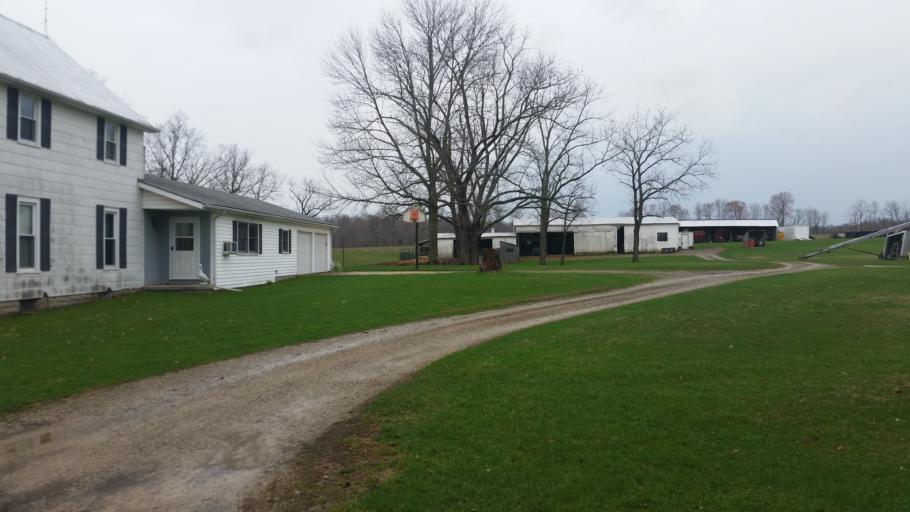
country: US
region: Ohio
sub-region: Knox County
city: Oak Hill
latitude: 40.3130
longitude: -82.2593
